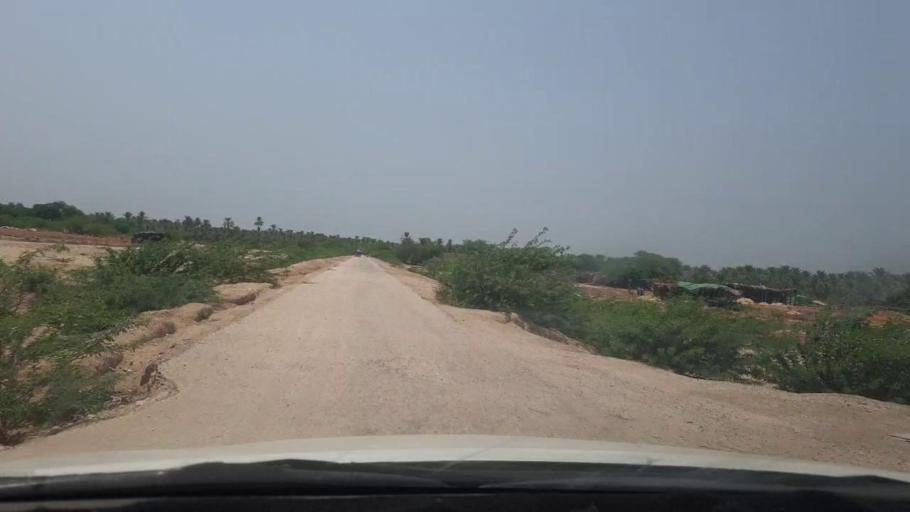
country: PK
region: Sindh
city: Khairpur
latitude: 27.4995
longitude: 68.8830
